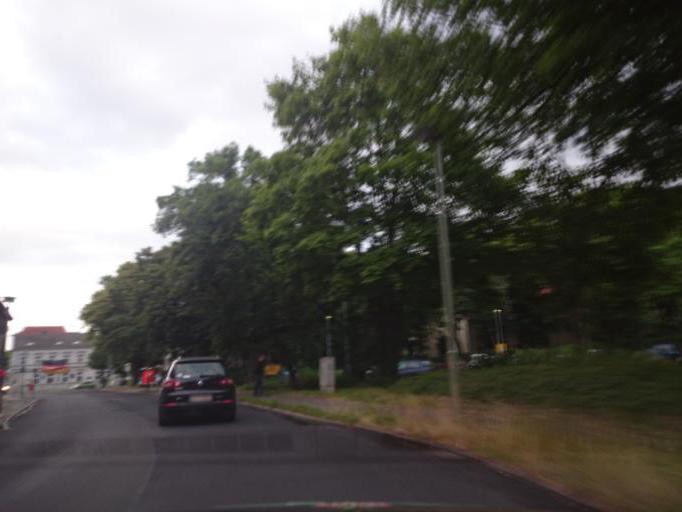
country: DE
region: Berlin
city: Altglienicke
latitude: 52.4225
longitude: 13.5399
